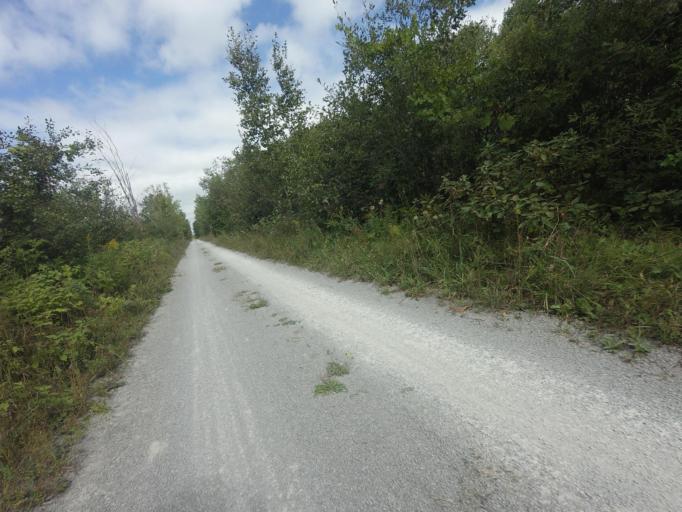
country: CA
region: Ontario
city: Uxbridge
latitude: 44.1688
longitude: -79.0771
